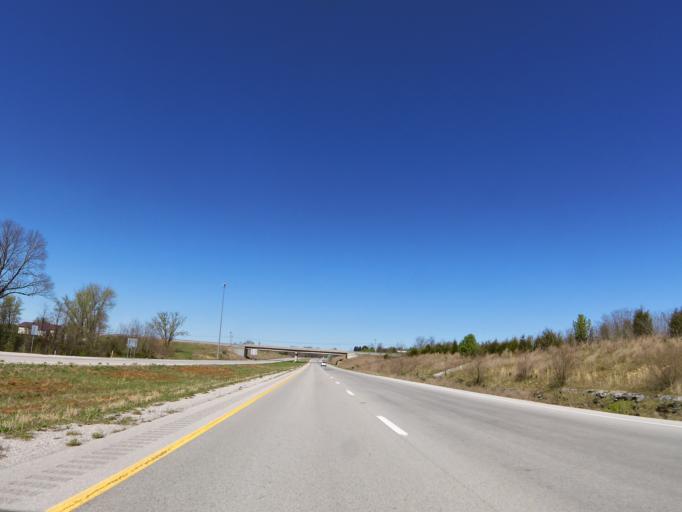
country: US
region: Kentucky
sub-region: Pulaski County
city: Somerset
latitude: 37.1089
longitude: -84.6588
